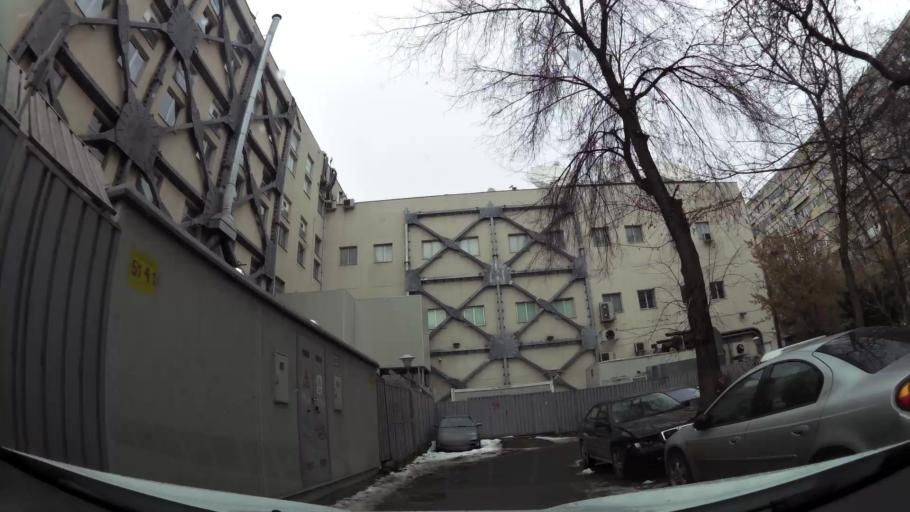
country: RO
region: Ilfov
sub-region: Comuna Chiajna
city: Rosu
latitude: 44.4210
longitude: 26.0383
